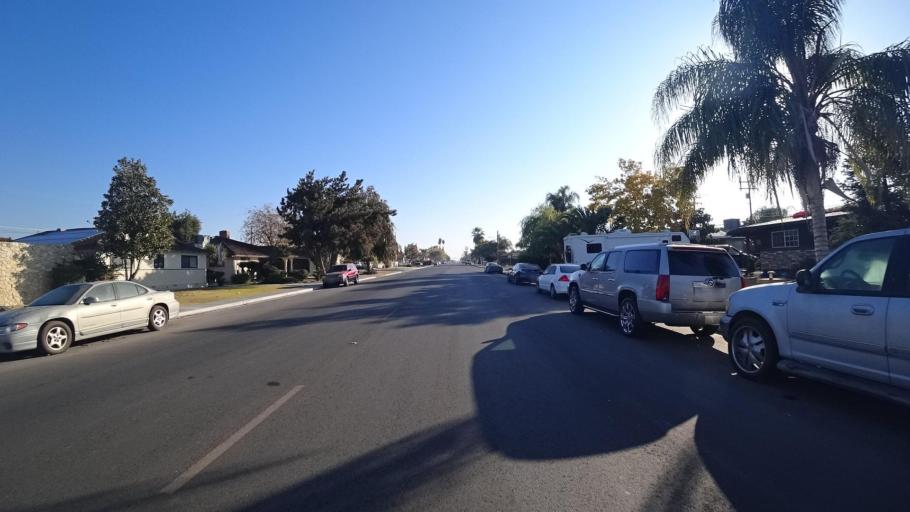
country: US
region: California
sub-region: Kern County
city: Delano
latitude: 35.7691
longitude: -119.2312
